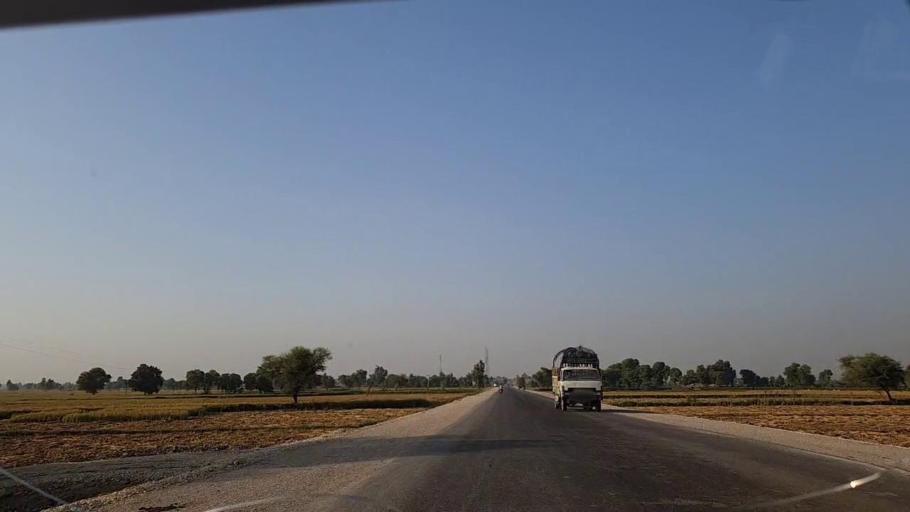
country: PK
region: Sindh
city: Rustam jo Goth
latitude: 27.9557
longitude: 68.8079
